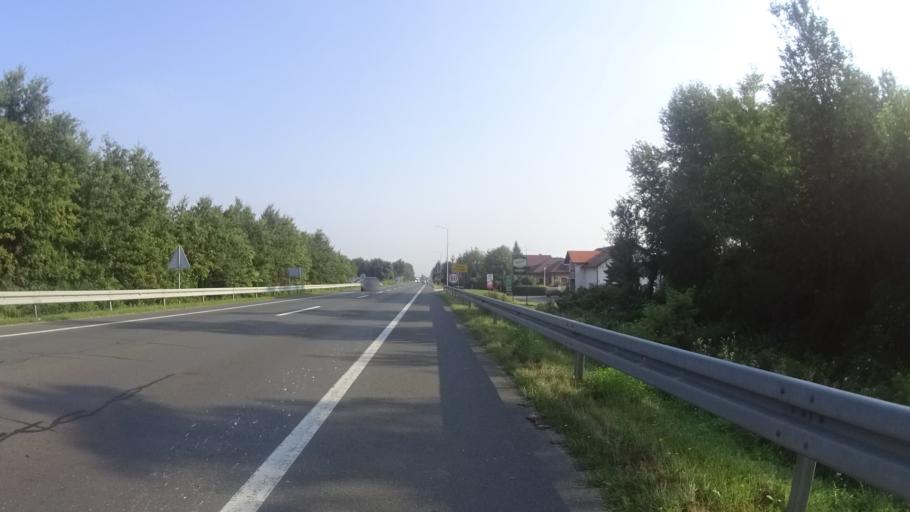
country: HR
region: Varazdinska
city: Varazdin
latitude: 46.3268
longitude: 16.3595
